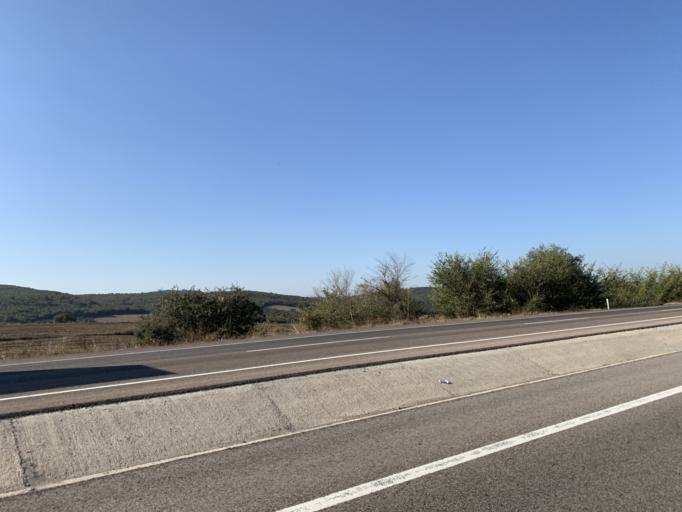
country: TR
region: Tekirdag
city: Yuruk
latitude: 40.9149
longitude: 27.1569
